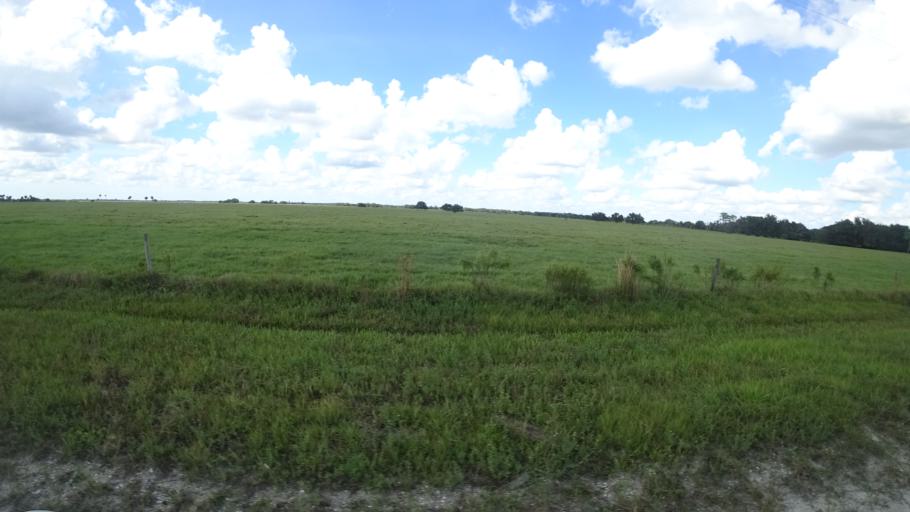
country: US
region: Florida
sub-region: Sarasota County
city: Warm Mineral Springs
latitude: 27.2592
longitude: -82.1592
